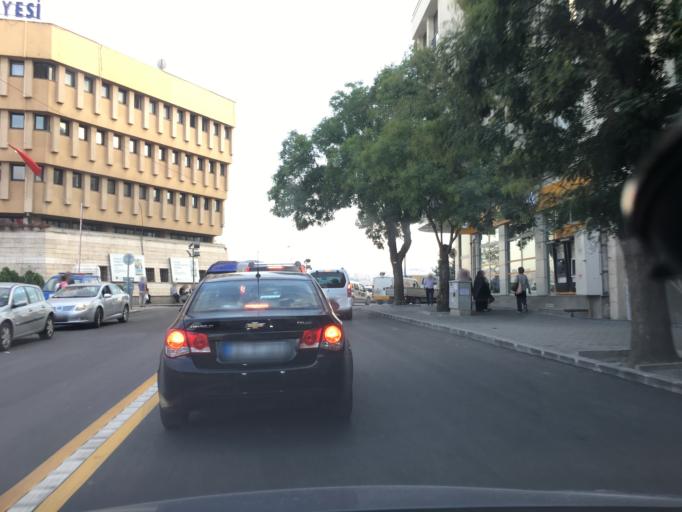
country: TR
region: Ankara
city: Ankara
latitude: 39.9348
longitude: 32.8619
